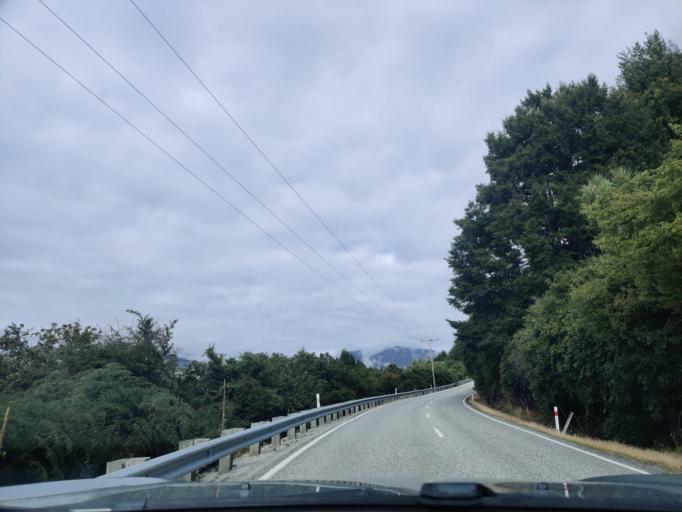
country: NZ
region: Otago
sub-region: Queenstown-Lakes District
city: Queenstown
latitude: -45.0749
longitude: 168.4946
